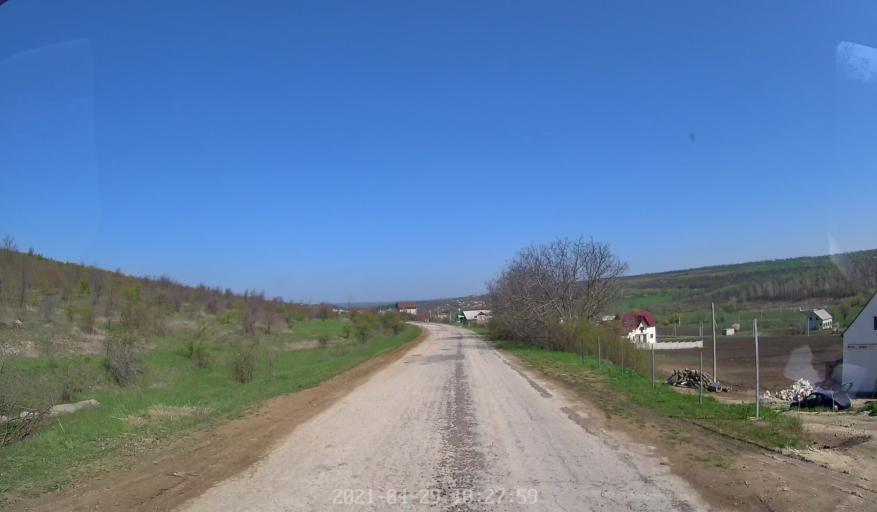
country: MD
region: Chisinau
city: Ciorescu
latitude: 47.1528
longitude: 28.9595
